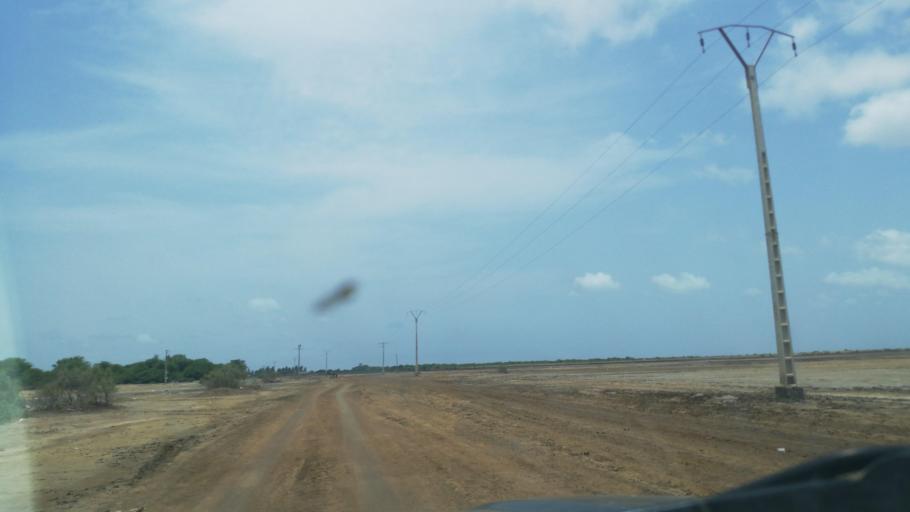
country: SN
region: Saint-Louis
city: Saint-Louis
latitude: 16.3475
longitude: -16.2763
